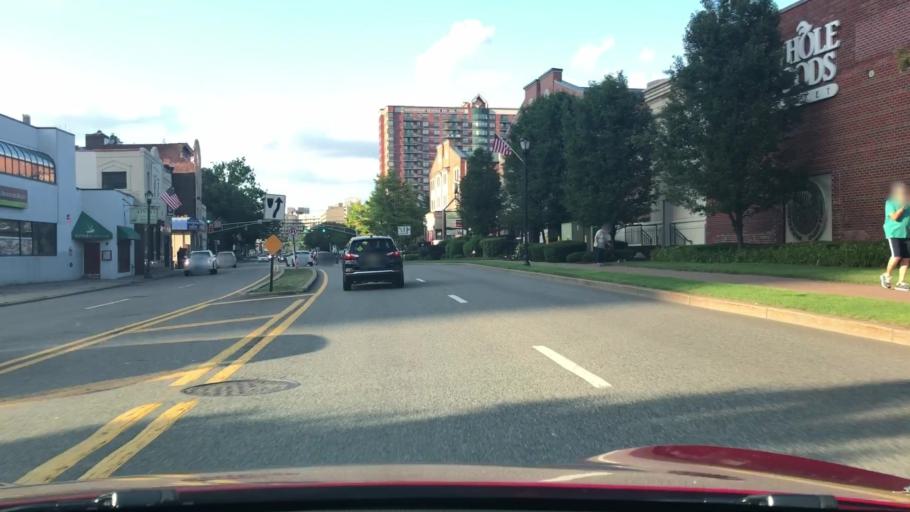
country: US
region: New Jersey
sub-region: Bergen County
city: Edgewater
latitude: 40.8249
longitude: -73.9746
